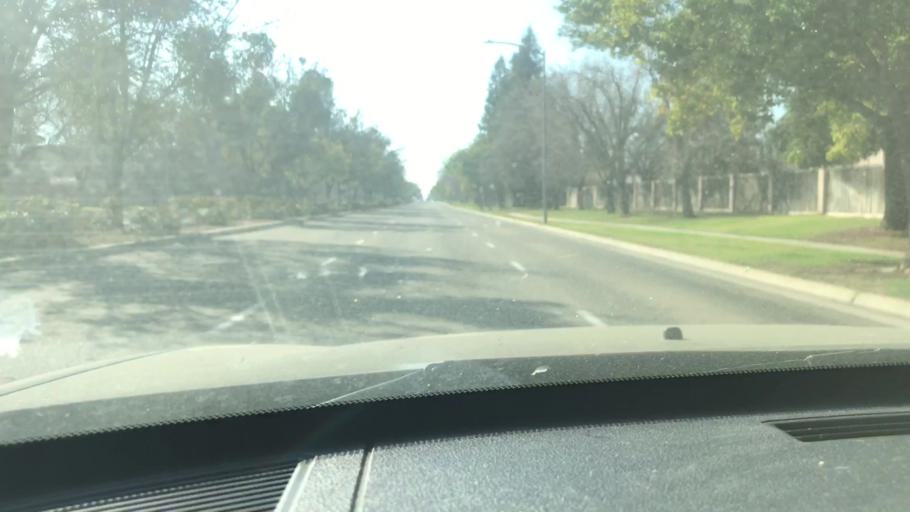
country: US
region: California
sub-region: Fresno County
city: Clovis
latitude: 36.8136
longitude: -119.6640
